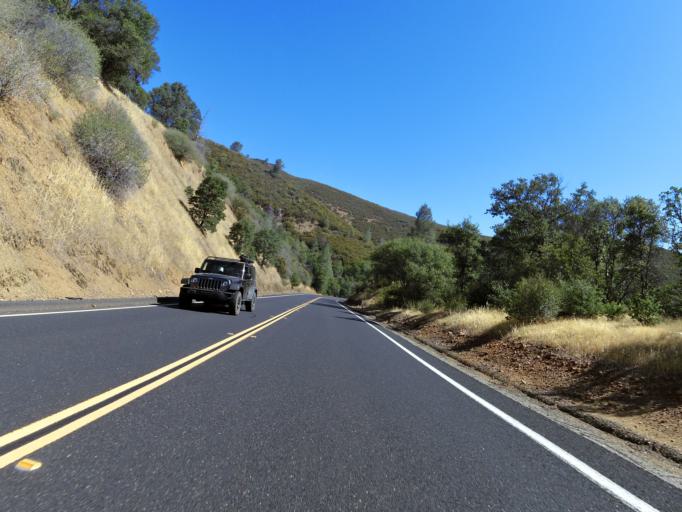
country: US
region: California
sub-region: Tuolumne County
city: Tuolumne City
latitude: 37.7076
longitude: -120.2259
